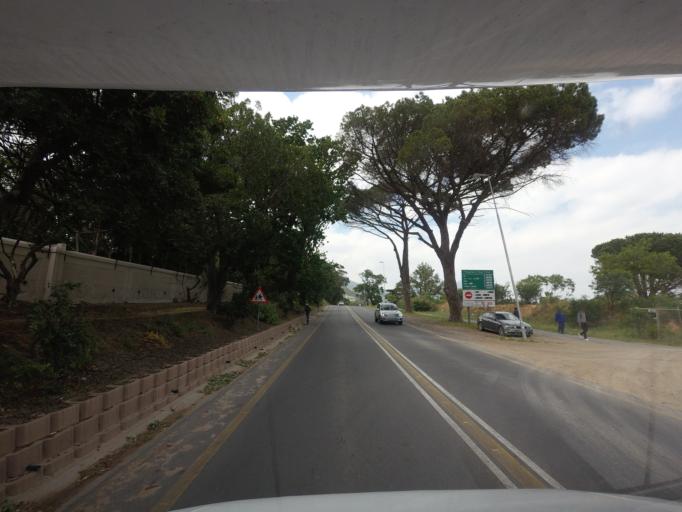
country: ZA
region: Western Cape
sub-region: City of Cape Town
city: Constantia
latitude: -34.0382
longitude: 18.3581
